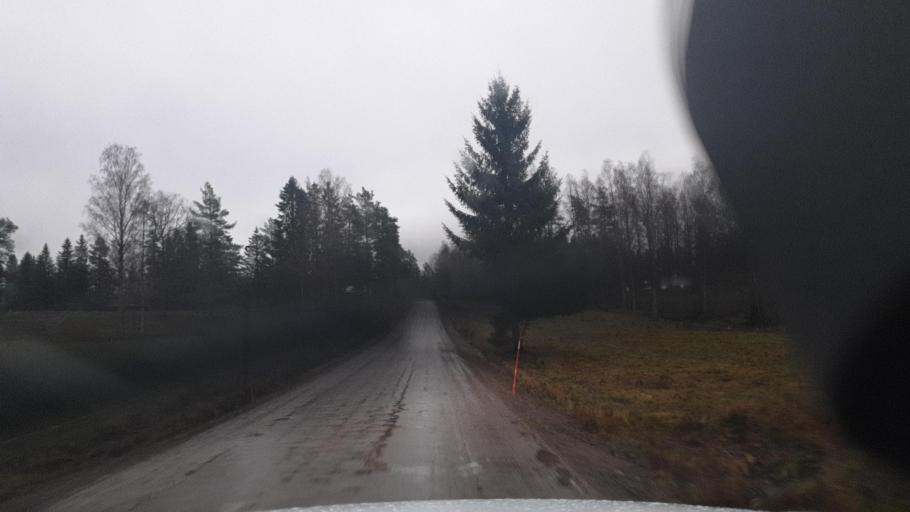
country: NO
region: Hedmark
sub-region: Eidskog
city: Skotterud
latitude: 59.7369
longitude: 12.0823
